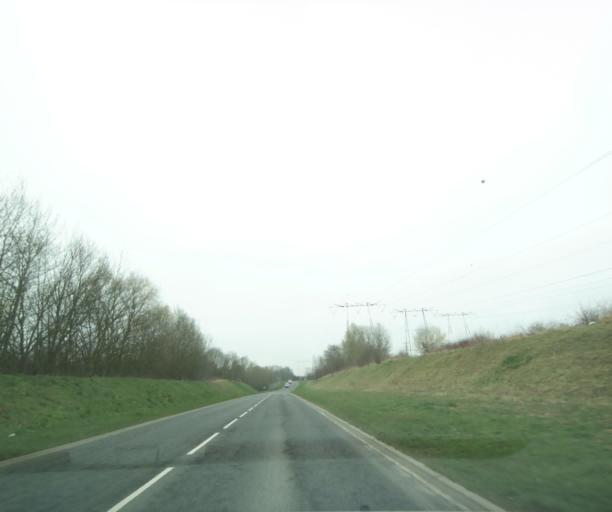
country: FR
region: Ile-de-France
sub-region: Departement du Val-d'Oise
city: Courdimanche
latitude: 49.0516
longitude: 2.0000
